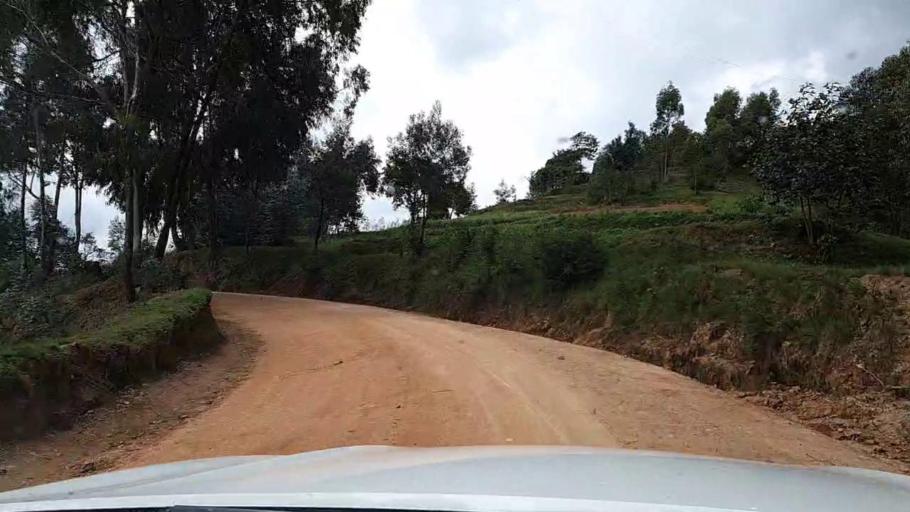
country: RW
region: Southern Province
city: Nzega
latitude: -2.4289
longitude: 29.4400
